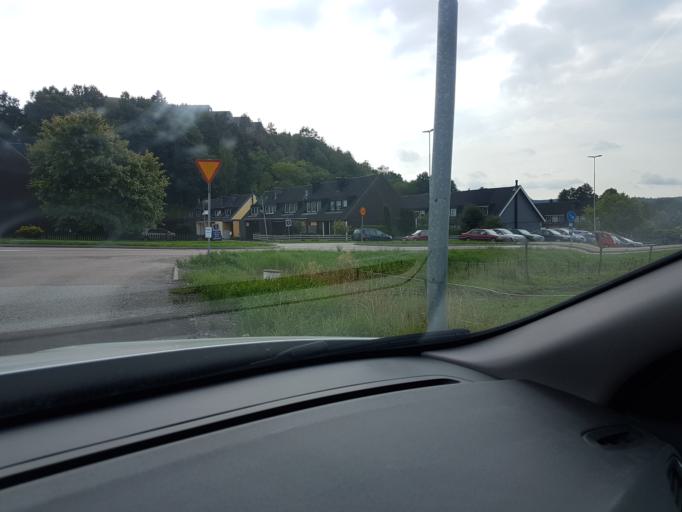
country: SE
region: Vaestra Goetaland
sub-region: Ale Kommun
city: Surte
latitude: 57.8533
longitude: 12.0292
